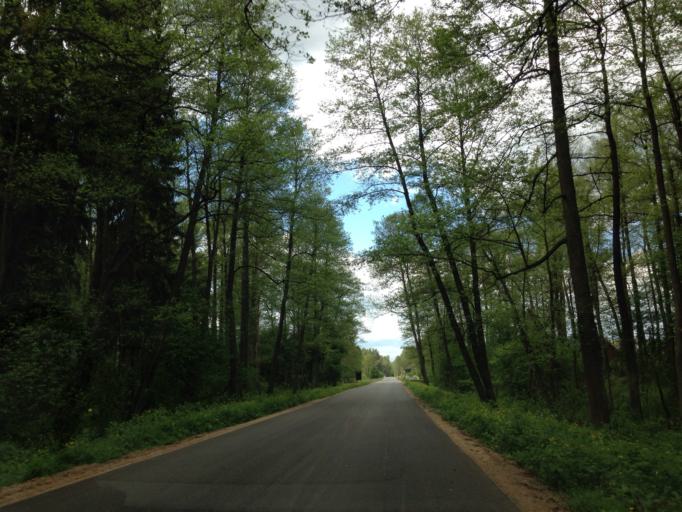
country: PL
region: Podlasie
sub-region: Powiat moniecki
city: Goniadz
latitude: 53.3675
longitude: 22.5933
